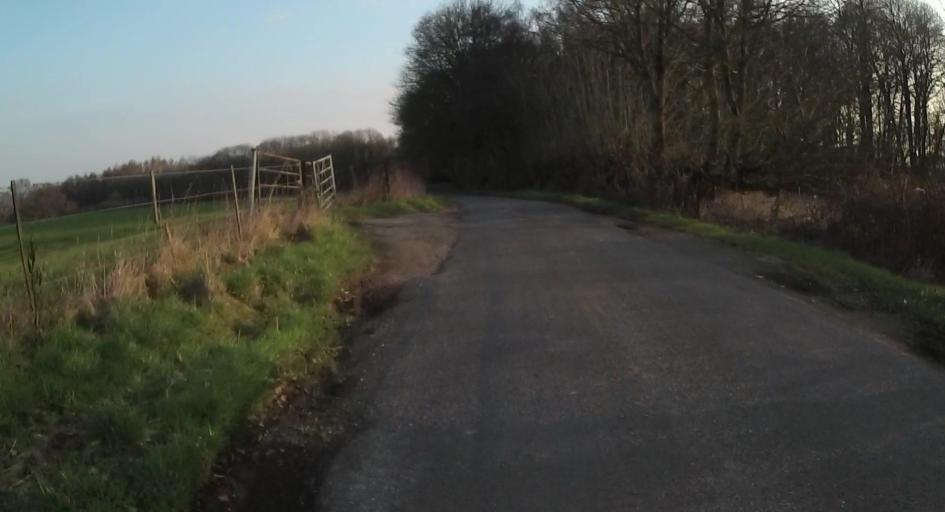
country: GB
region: England
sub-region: Hampshire
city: Alton
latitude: 51.1619
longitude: -0.9989
